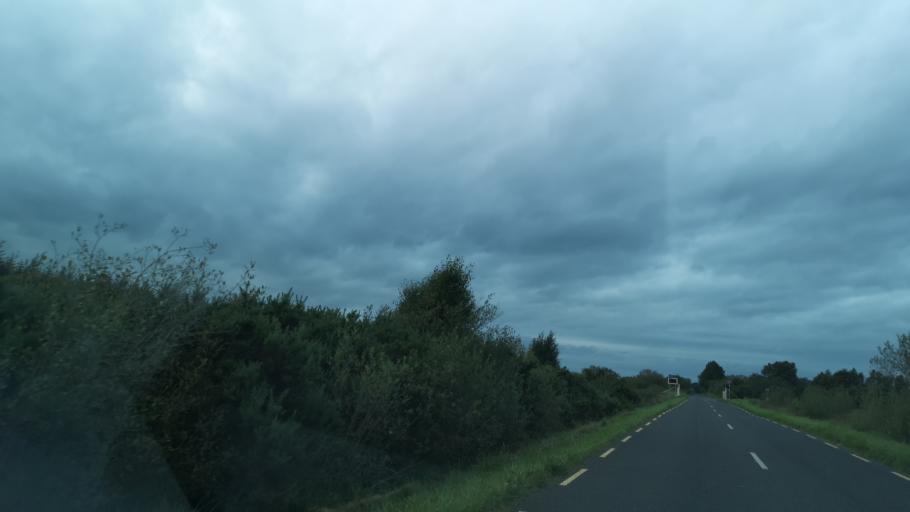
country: IE
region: Leinster
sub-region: Uibh Fhaili
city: Ferbane
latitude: 53.2095
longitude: -7.7874
